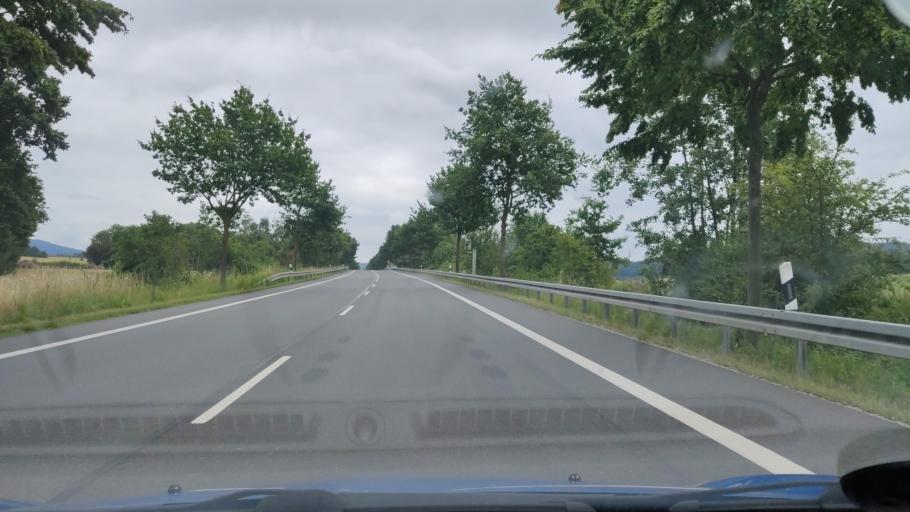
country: DE
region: Lower Saxony
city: Dielmissen
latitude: 51.9624
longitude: 9.6020
